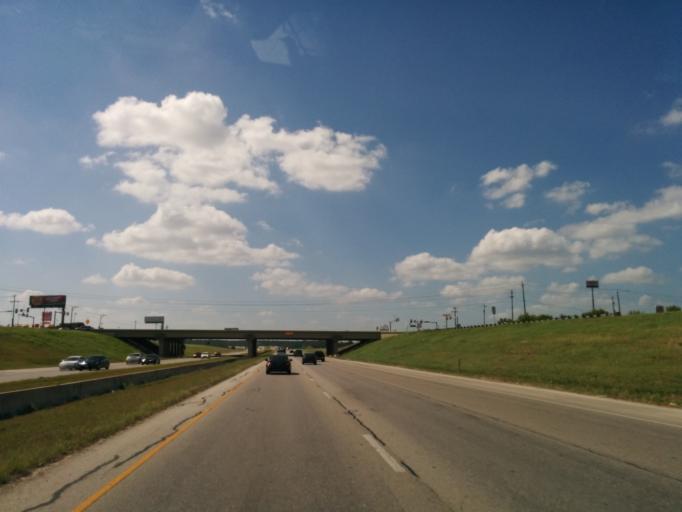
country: US
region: Texas
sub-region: Bexar County
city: Live Oak
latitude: 29.5904
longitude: -98.3508
